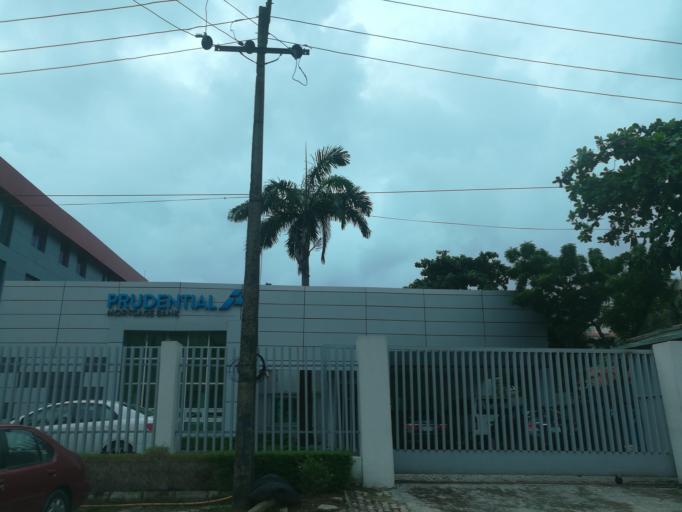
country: NG
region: Lagos
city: Ikoyi
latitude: 6.4240
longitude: 3.4214
